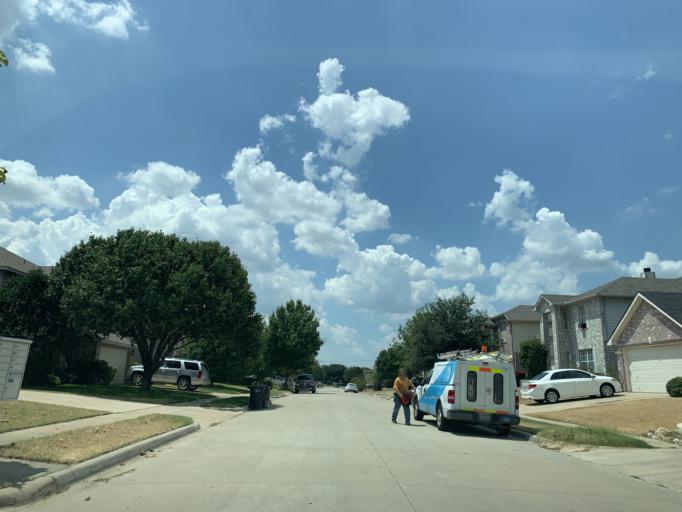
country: US
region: Texas
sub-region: Tarrant County
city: White Settlement
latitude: 32.7278
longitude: -97.5011
